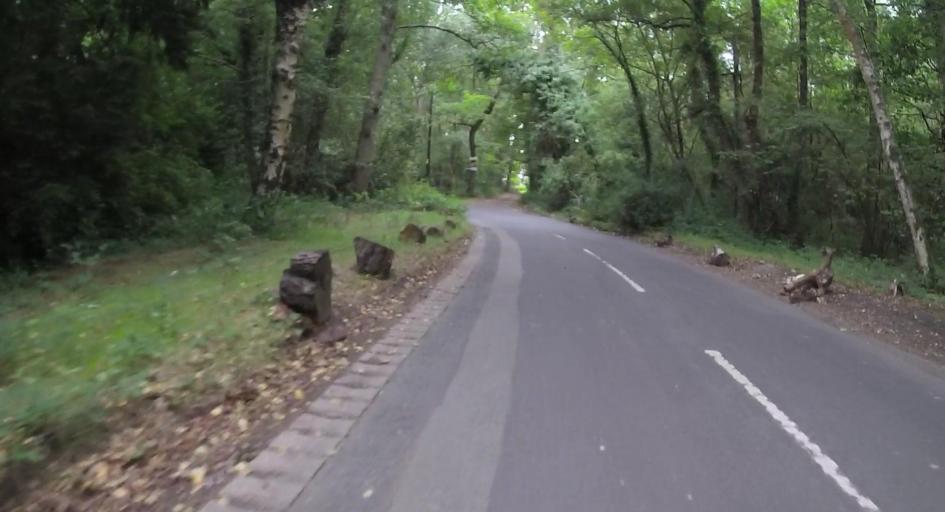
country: GB
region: England
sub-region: Surrey
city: Knaphill
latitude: 51.3315
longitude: -0.6469
